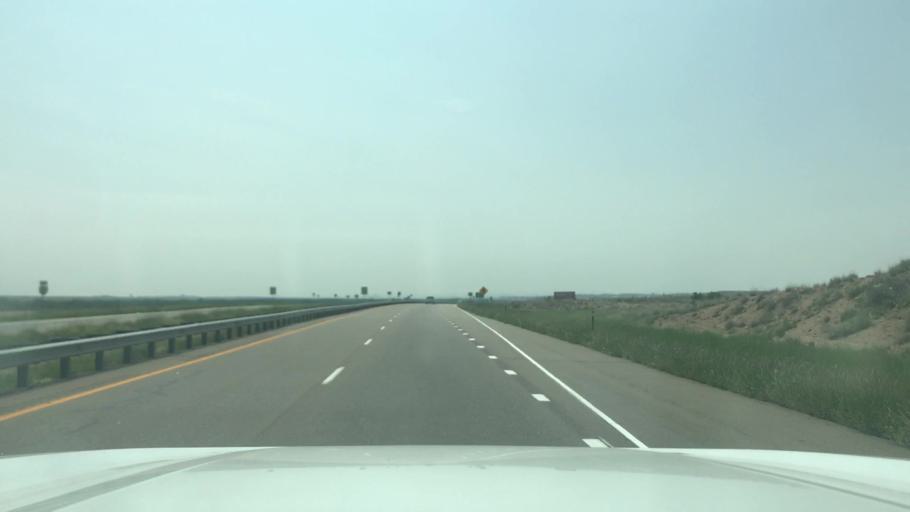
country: US
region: Colorado
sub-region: Pueblo County
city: Pueblo West
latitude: 38.3859
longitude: -104.6193
